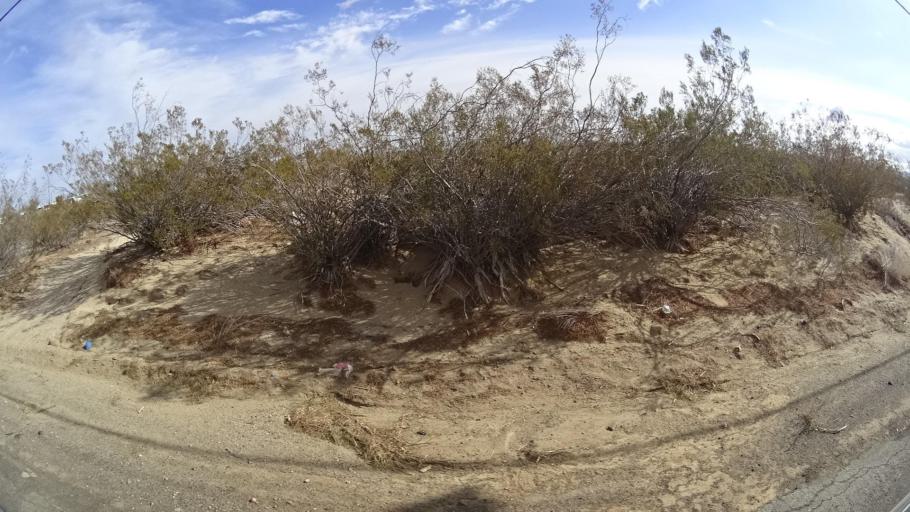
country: US
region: California
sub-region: Kern County
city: Mojave
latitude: 35.0593
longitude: -118.1946
